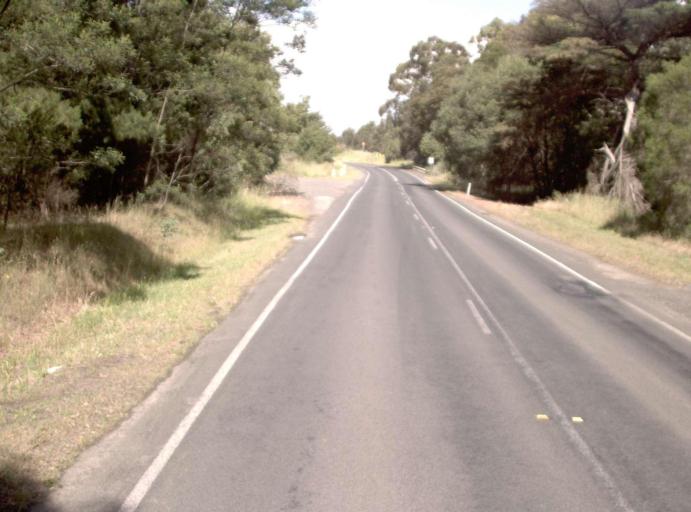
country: AU
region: Victoria
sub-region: Latrobe
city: Morwell
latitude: -38.1593
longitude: 146.4126
